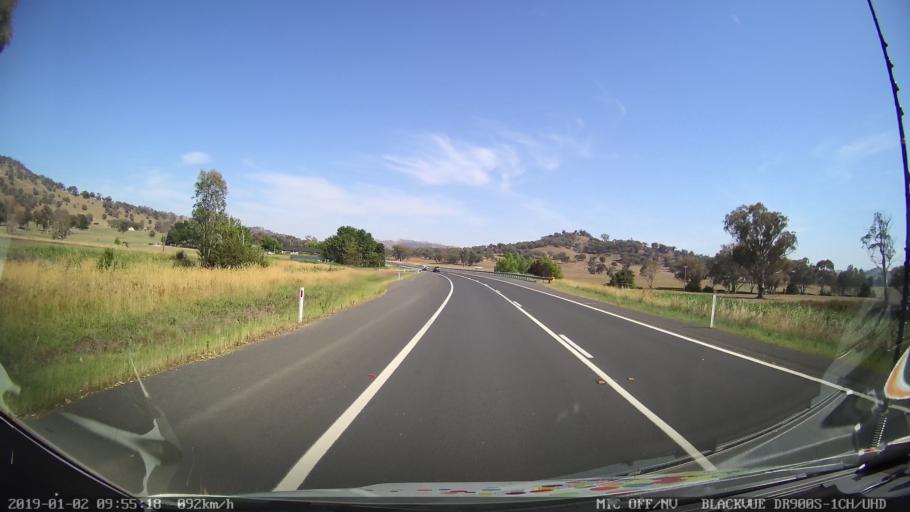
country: AU
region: New South Wales
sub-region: Tumut Shire
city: Tumut
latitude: -35.2248
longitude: 148.1901
